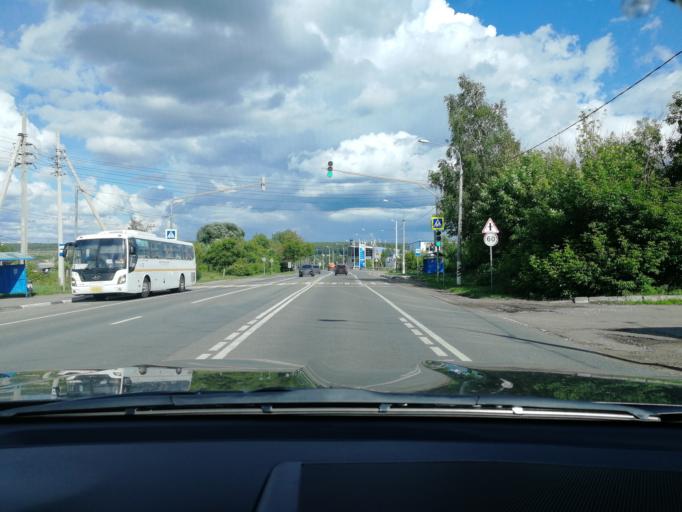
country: RU
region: Moskovskaya
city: Serpukhov
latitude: 54.9117
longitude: 37.4749
